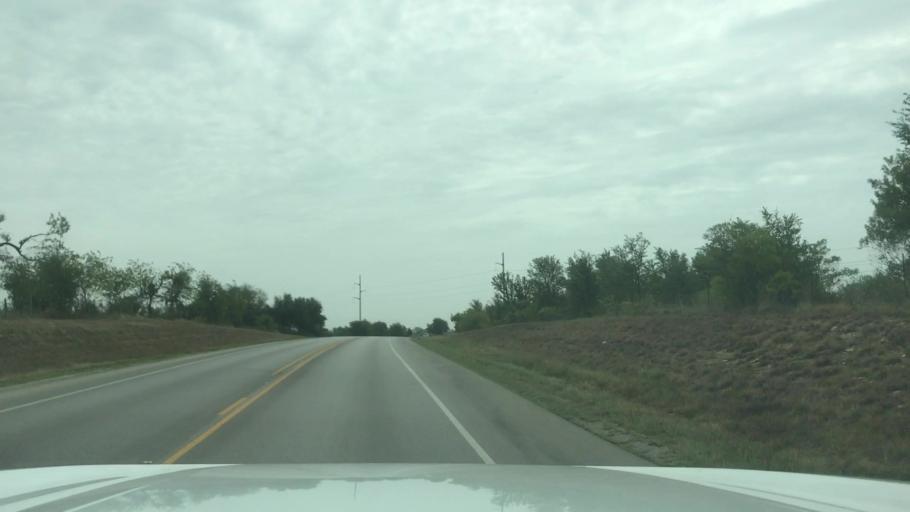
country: US
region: Texas
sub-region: Erath County
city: Dublin
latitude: 32.0976
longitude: -98.3840
